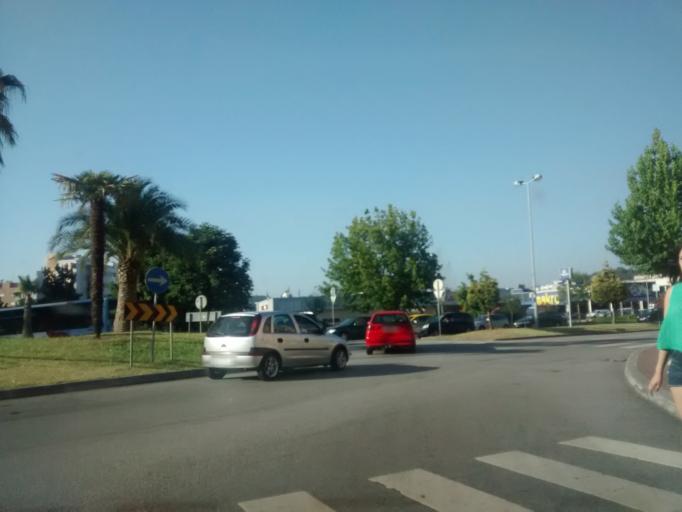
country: PT
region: Braga
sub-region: Braga
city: Braga
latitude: 41.5482
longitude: -8.4030
